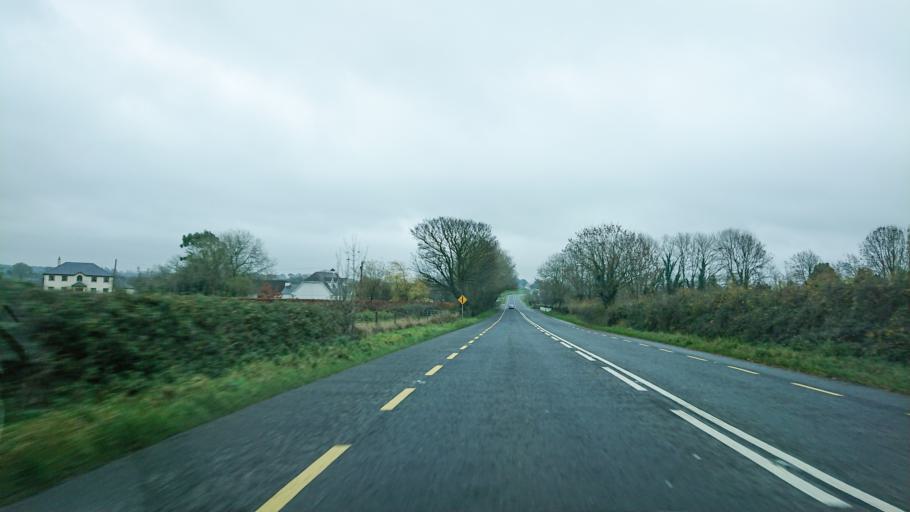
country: IE
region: Leinster
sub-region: Kilkenny
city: Mooncoin
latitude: 52.2864
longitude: -7.2182
